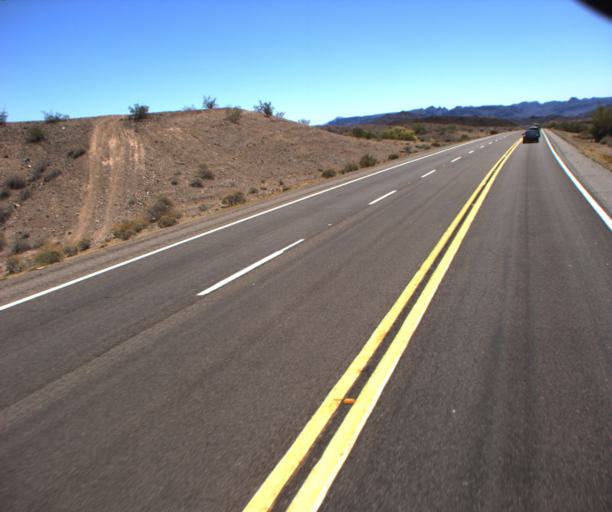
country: US
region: Arizona
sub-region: Mohave County
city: Lake Havasu City
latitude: 34.3873
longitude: -114.1679
